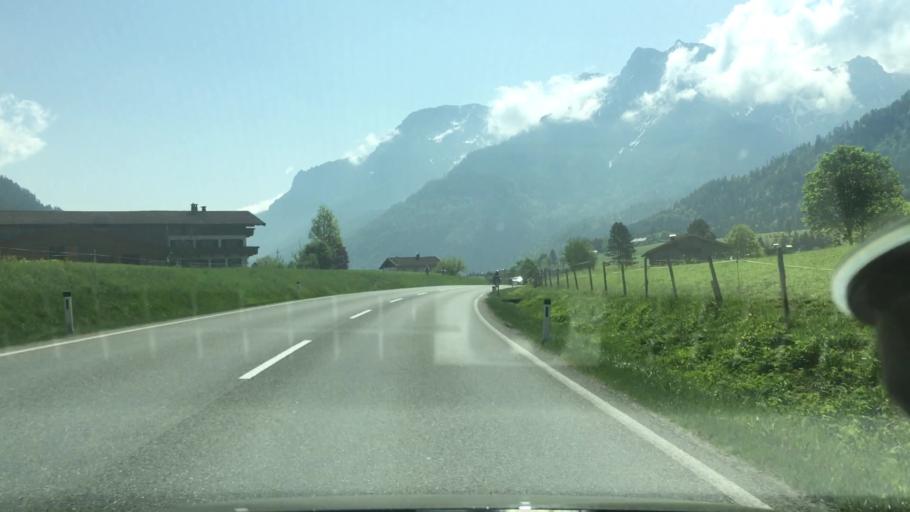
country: AT
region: Tyrol
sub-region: Politischer Bezirk Kitzbuhel
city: Waidring
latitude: 47.5919
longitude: 12.5485
